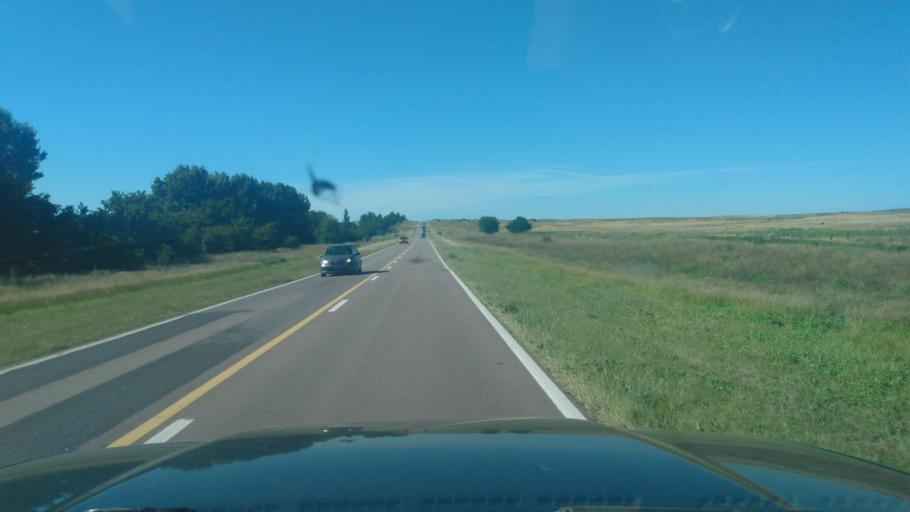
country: AR
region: La Pampa
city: Doblas
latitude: -37.2854
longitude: -64.2875
